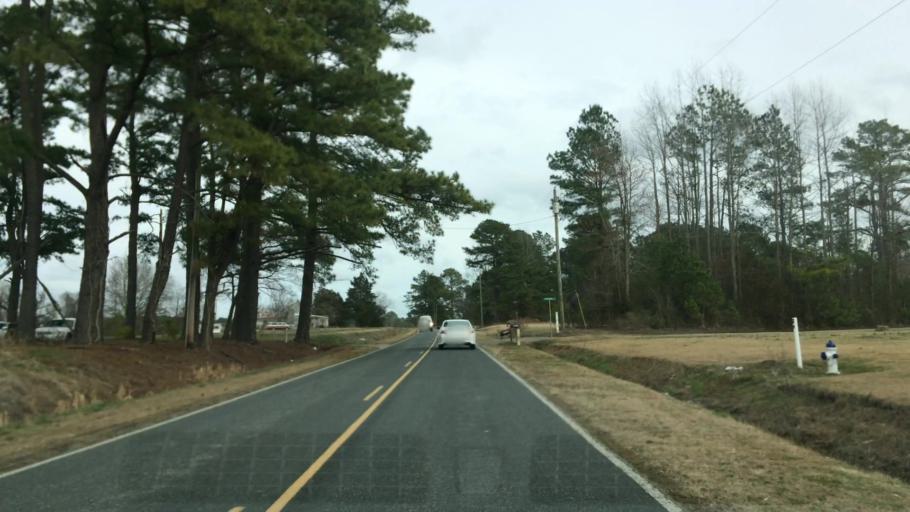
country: US
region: North Carolina
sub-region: Pitt County
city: Winterville
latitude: 35.4894
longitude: -77.3628
